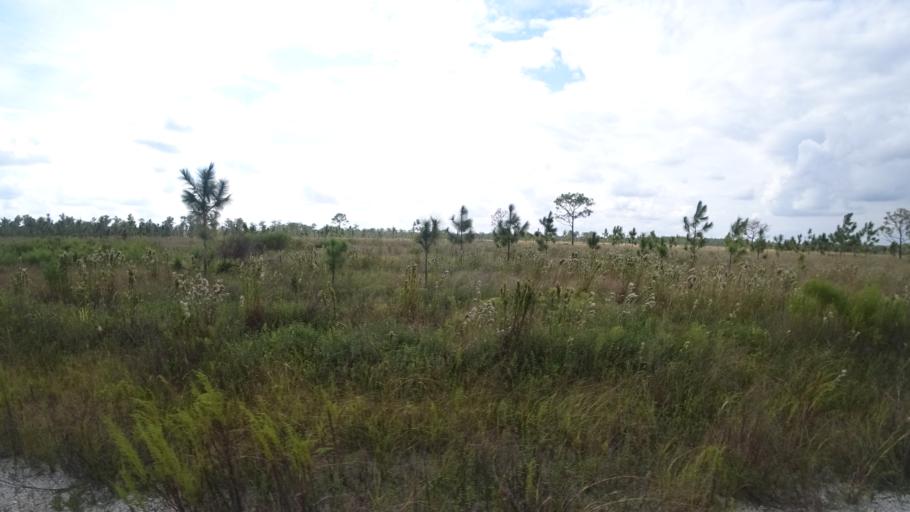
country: US
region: Florida
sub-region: Hillsborough County
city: Wimauma
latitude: 27.5336
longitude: -82.1291
